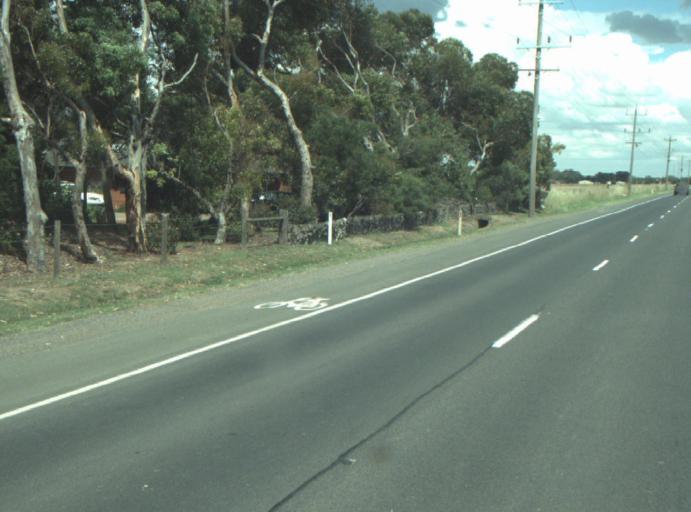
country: AU
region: Victoria
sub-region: Greater Geelong
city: Leopold
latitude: -38.1739
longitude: 144.4533
